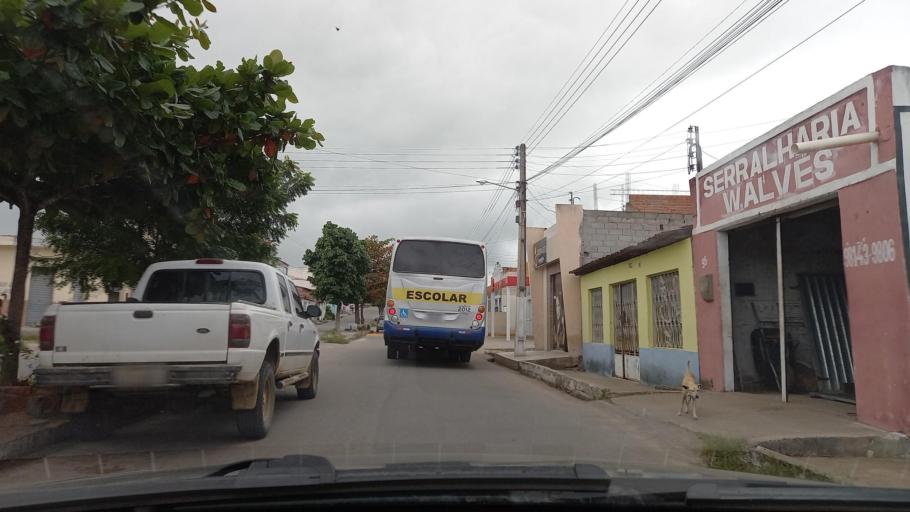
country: BR
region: Sergipe
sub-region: Caninde De Sao Francisco
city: Caninde de Sao Francisco
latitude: -9.6063
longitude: -37.7594
